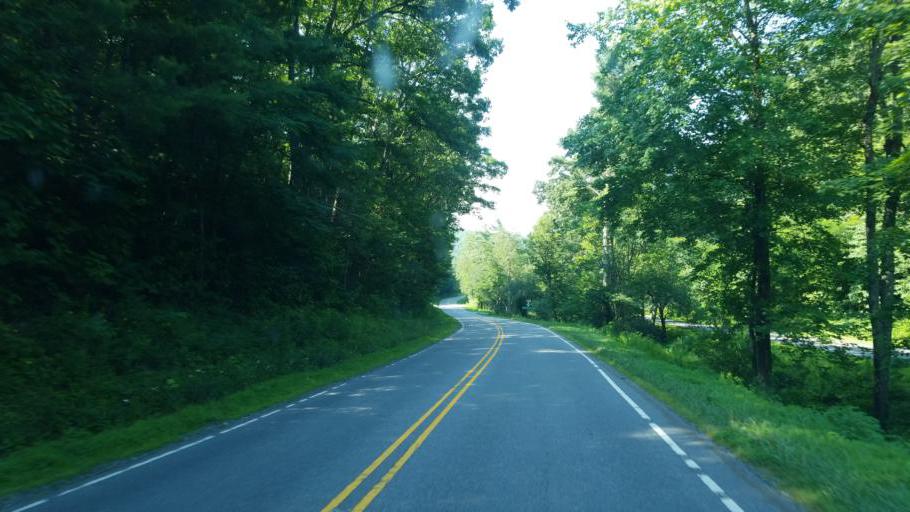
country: US
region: North Carolina
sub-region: Avery County
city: Newland
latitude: 35.9962
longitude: -81.8906
